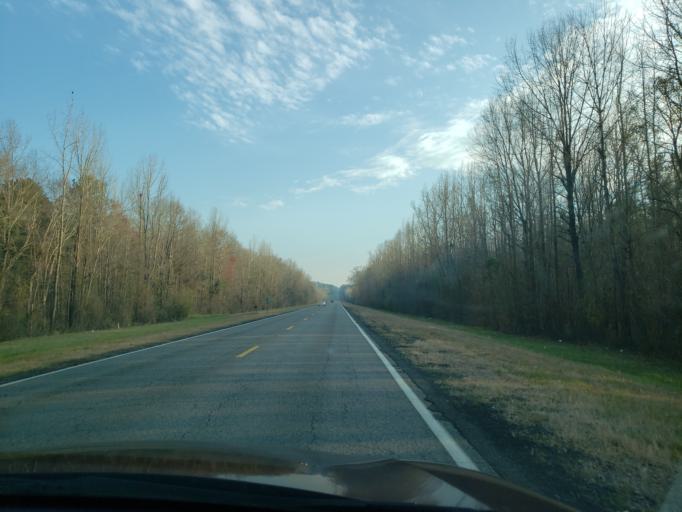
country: US
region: Alabama
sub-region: Hale County
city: Greensboro
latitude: 32.7701
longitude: -87.5855
